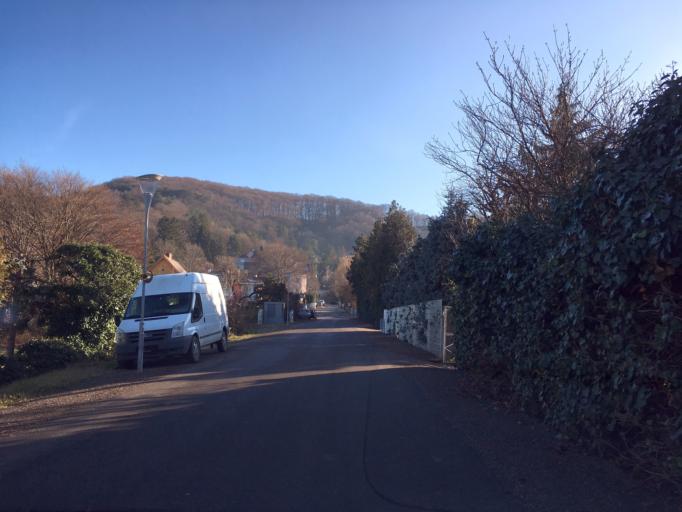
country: AT
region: Lower Austria
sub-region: Politischer Bezirk Tulln
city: Wordern
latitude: 48.3262
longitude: 16.2135
